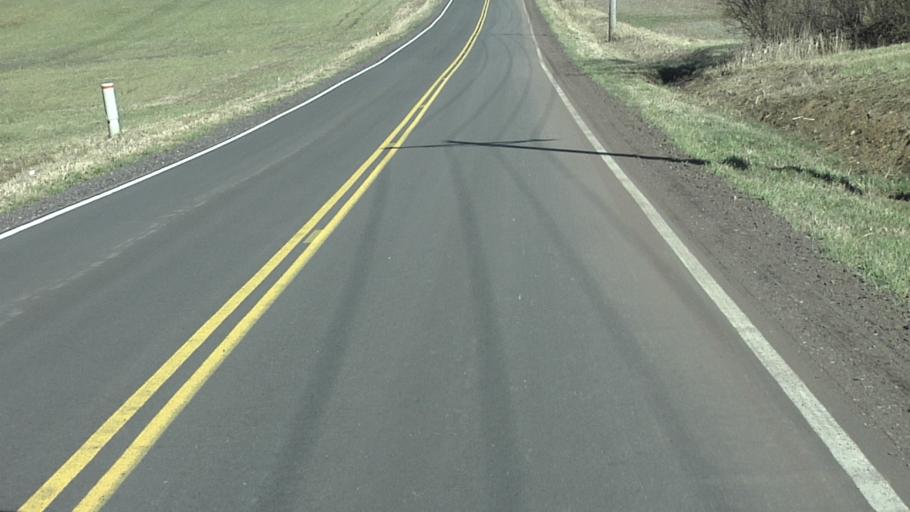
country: US
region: Ohio
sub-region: Richland County
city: Shelby
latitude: 40.8954
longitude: -82.7437
